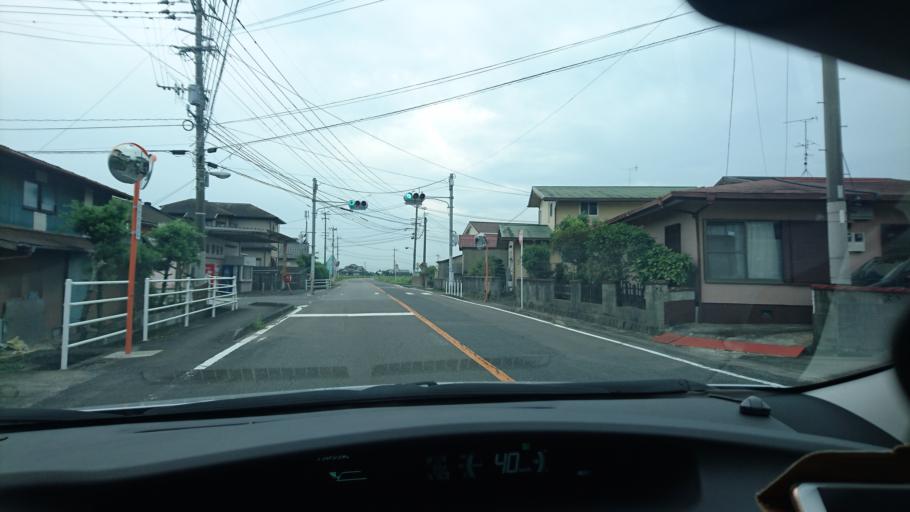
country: JP
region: Saga Prefecture
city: Takeocho-takeo
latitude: 33.2086
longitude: 130.1216
